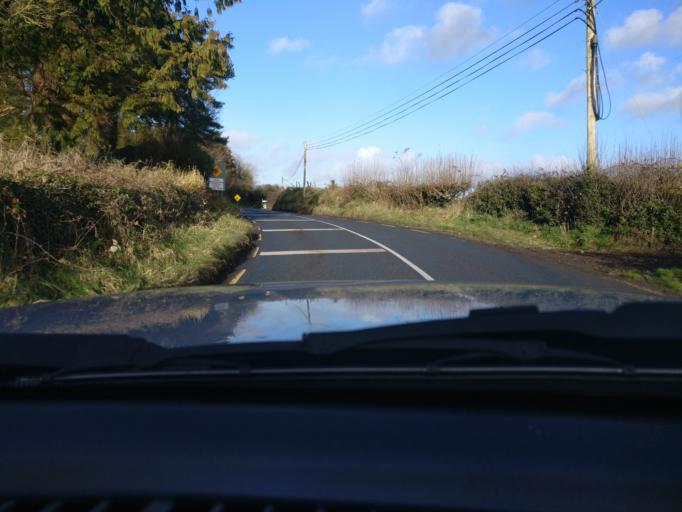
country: IE
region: Leinster
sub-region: Uibh Fhaili
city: Clara
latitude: 53.3973
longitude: -7.5811
